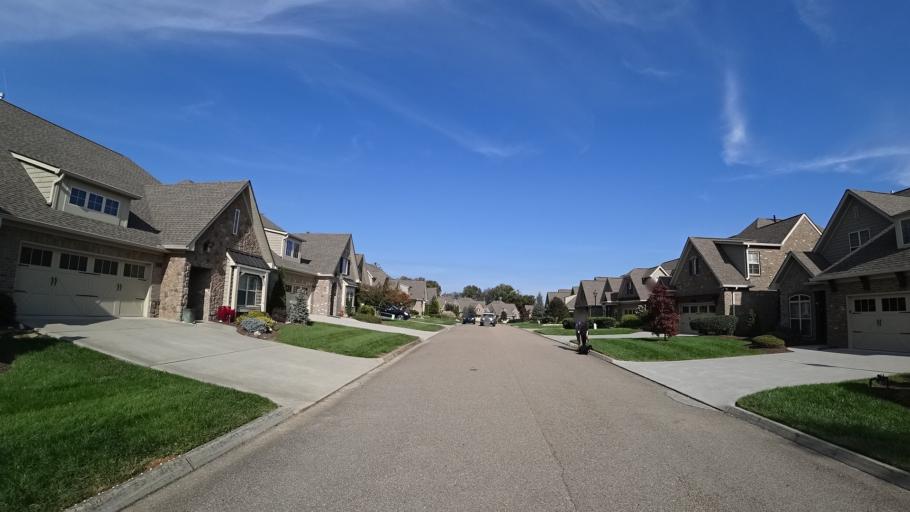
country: US
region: Tennessee
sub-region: Knox County
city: Farragut
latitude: 35.9231
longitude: -84.1572
